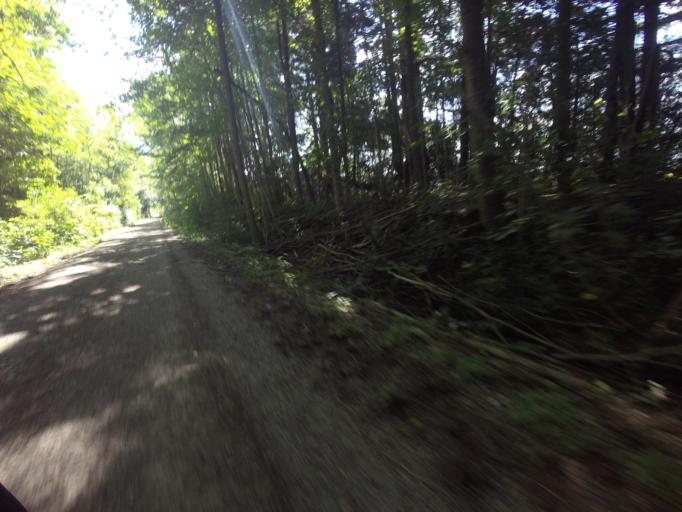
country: CA
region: Ontario
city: Huron East
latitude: 43.6920
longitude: -81.3279
